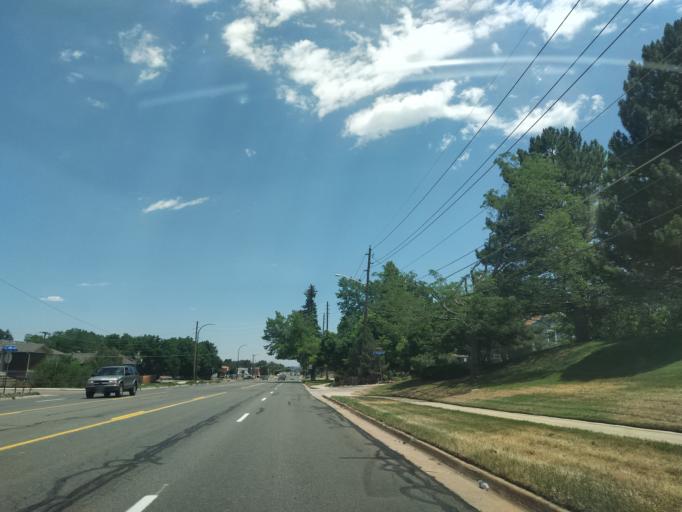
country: US
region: Colorado
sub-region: Jefferson County
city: Lakewood
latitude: 39.6821
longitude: -105.0890
